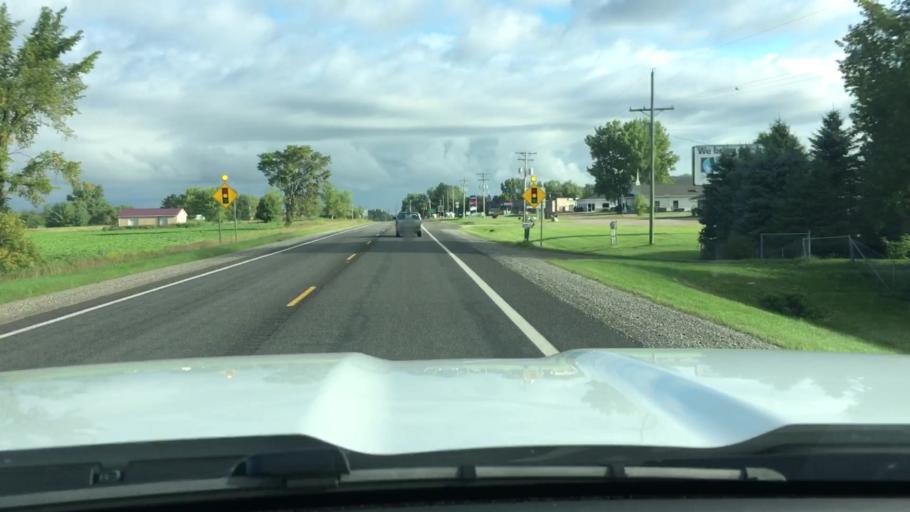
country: US
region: Michigan
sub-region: Tuscola County
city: Caro
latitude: 43.4052
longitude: -83.3837
